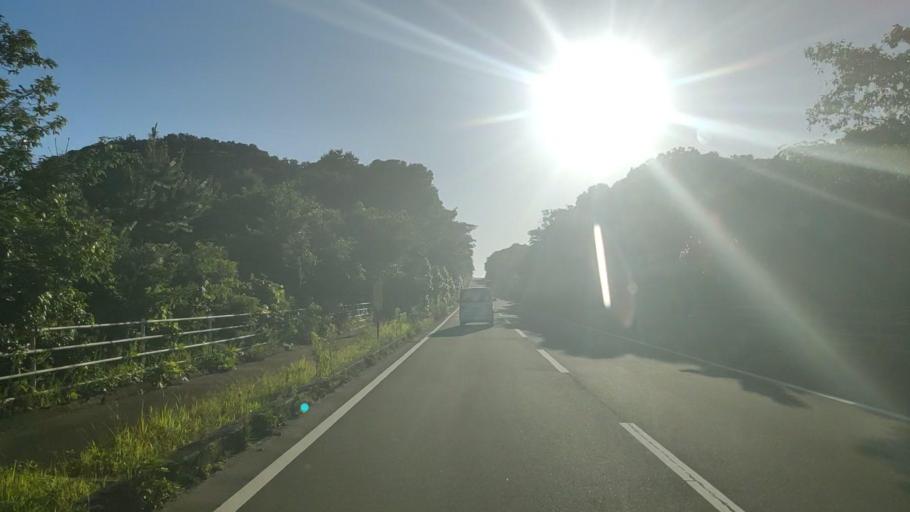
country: JP
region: Mie
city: Toba
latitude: 34.2686
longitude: 136.8019
